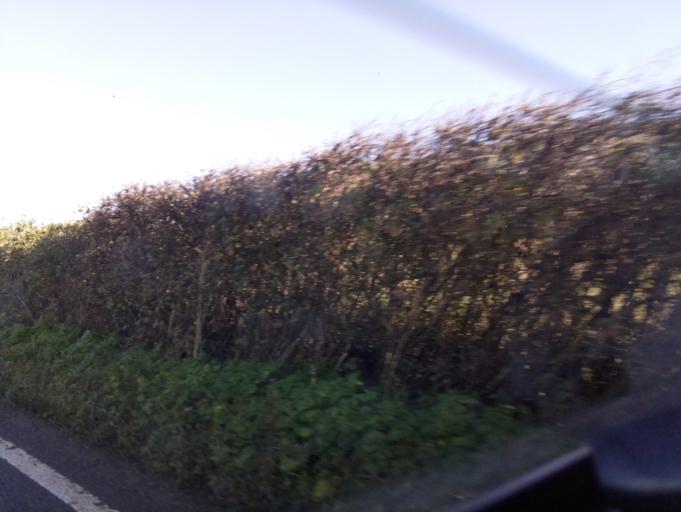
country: GB
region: England
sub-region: Somerset
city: Langport
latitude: 51.0689
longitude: -2.8558
